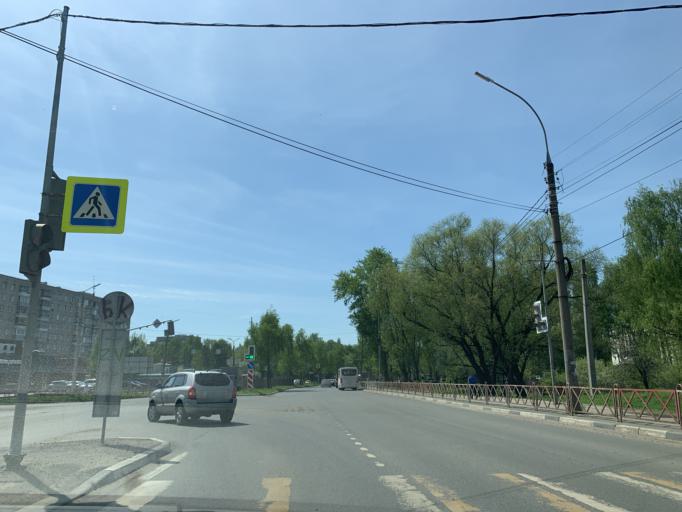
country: RU
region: Jaroslavl
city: Yaroslavl
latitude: 57.6549
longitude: 39.9425
